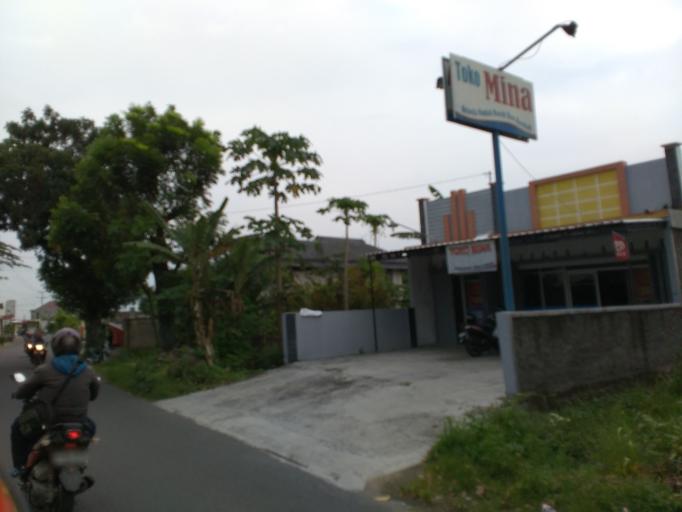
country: ID
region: Central Java
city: Delanggu
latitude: -7.5924
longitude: 110.6521
